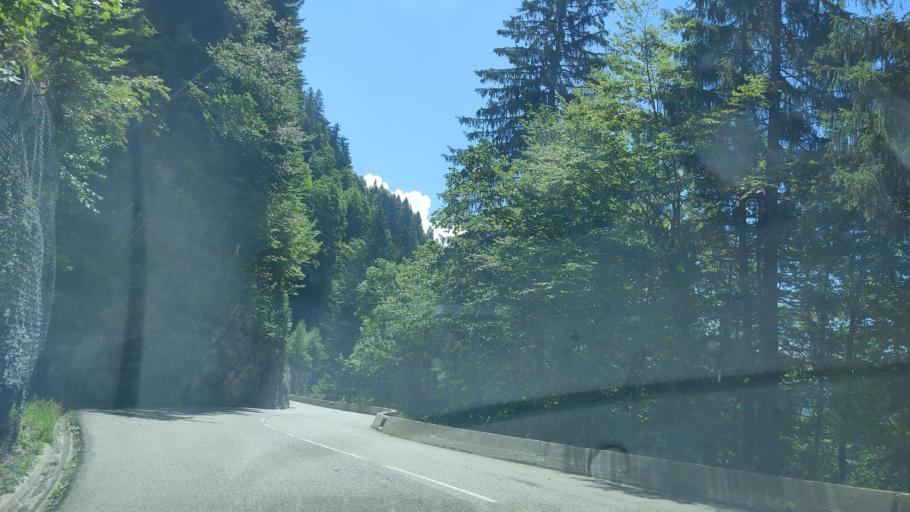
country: FR
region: Rhone-Alpes
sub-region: Departement de la Haute-Savoie
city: Praz-sur-Arly
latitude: 45.8305
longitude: 6.5092
